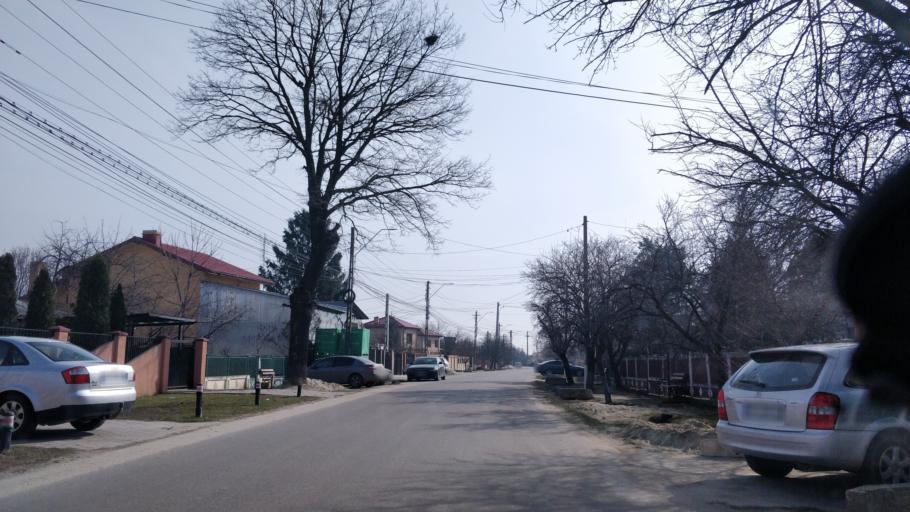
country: RO
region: Giurgiu
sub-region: Comuna Ulmi
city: Ulmi
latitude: 44.4860
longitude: 25.7829
